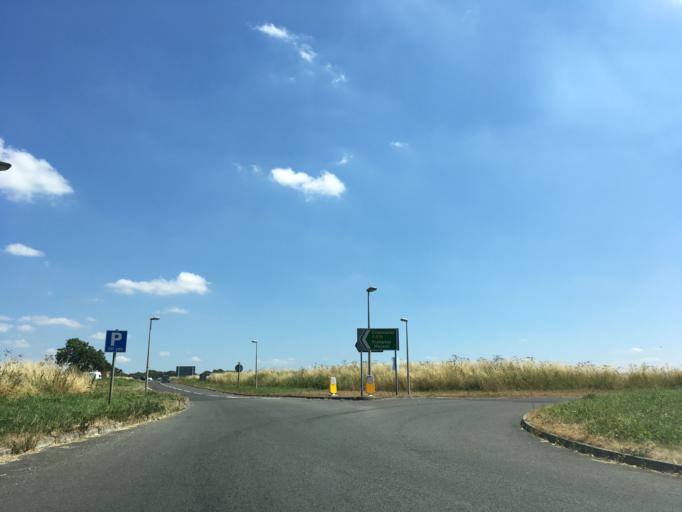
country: GB
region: England
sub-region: Gloucestershire
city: Chalford
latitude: 51.7156
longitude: -2.1329
